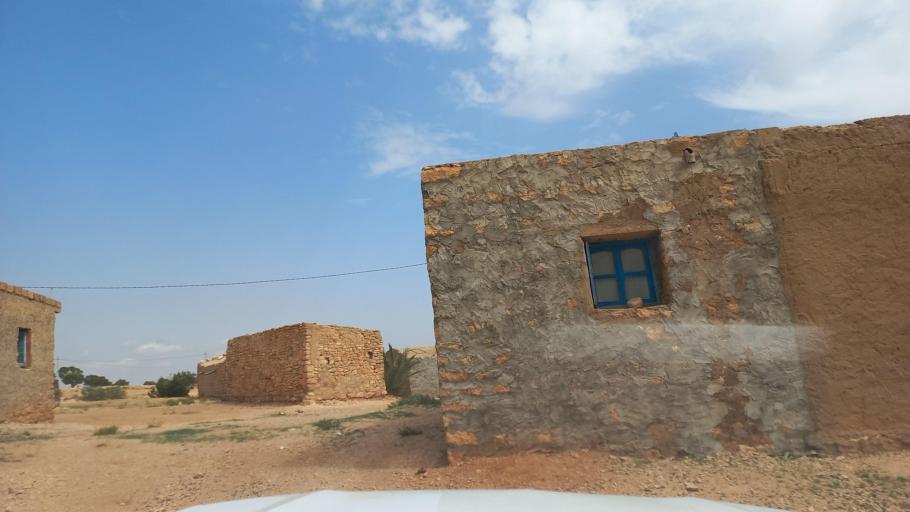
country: TN
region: Al Qasrayn
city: Kasserine
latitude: 35.3695
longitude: 8.8958
